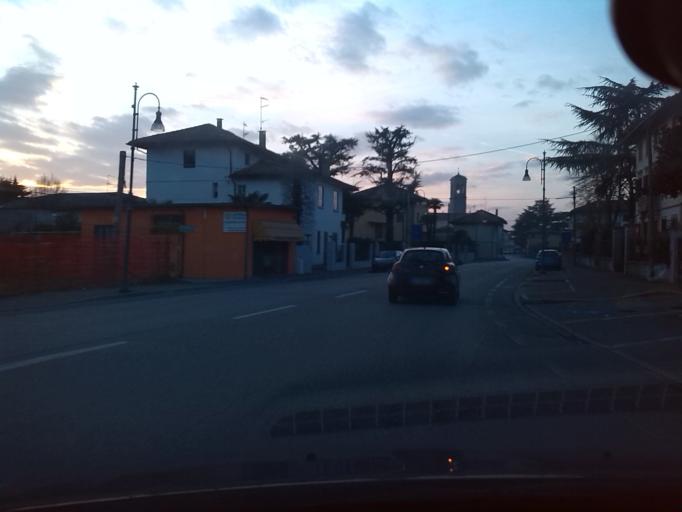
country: IT
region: Friuli Venezia Giulia
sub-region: Provincia di Udine
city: Zugliano-Terenzano-Cargnacco
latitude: 46.0161
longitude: 13.2116
